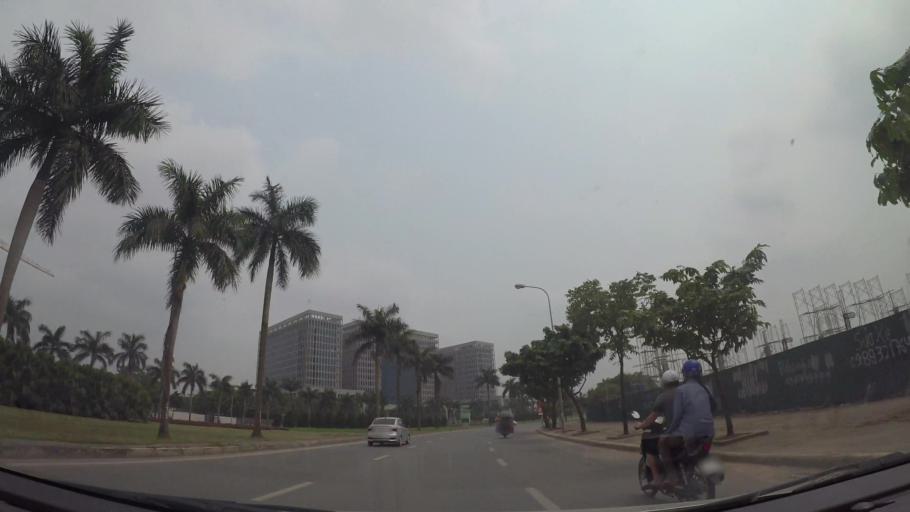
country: VN
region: Ha Noi
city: Thanh Xuan
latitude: 21.0087
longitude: 105.7732
